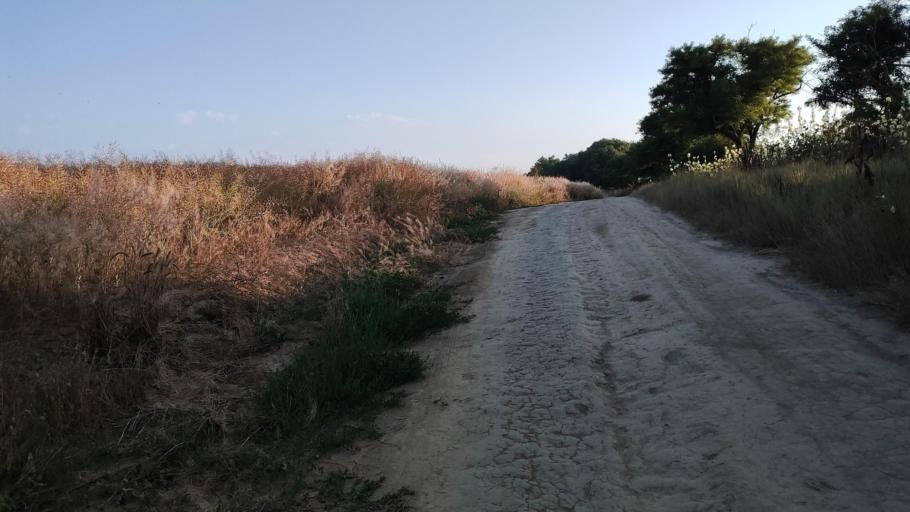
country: RU
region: Krasnodarskiy
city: Blagovetschenskaya
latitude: 45.0694
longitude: 37.0567
